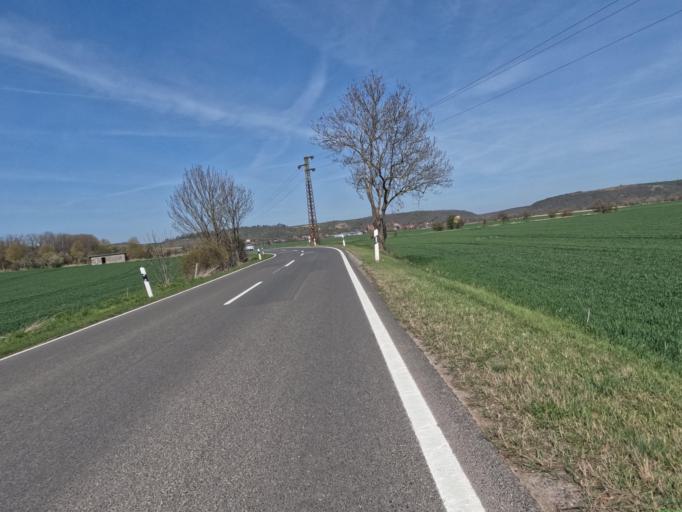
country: DE
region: Saxony-Anhalt
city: Beesenstedt
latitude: 51.6045
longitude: 11.7484
